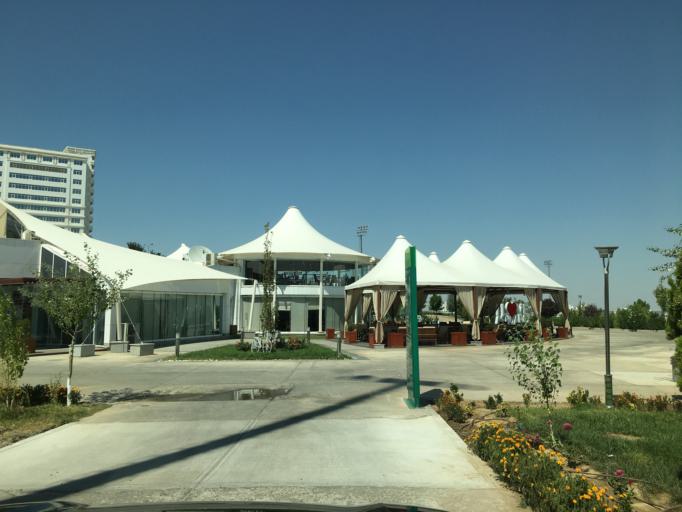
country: TM
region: Ahal
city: Ashgabat
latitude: 37.9277
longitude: 58.3470
